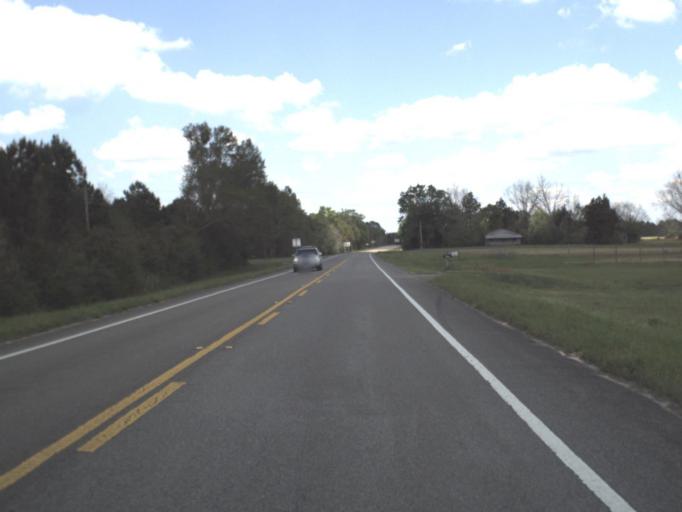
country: US
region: Florida
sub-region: Okaloosa County
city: Crestview
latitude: 30.9863
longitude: -86.6296
